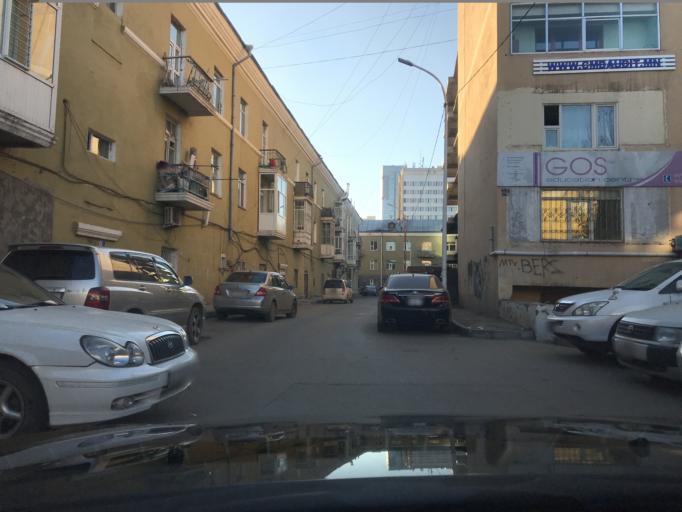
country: MN
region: Ulaanbaatar
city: Ulaanbaatar
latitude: 47.9226
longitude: 106.9101
